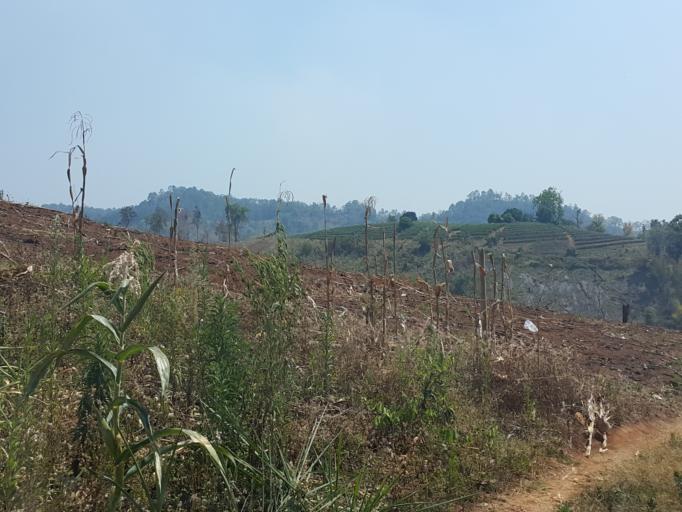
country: TH
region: Chiang Mai
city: Samoeng
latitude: 18.8894
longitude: 98.7717
